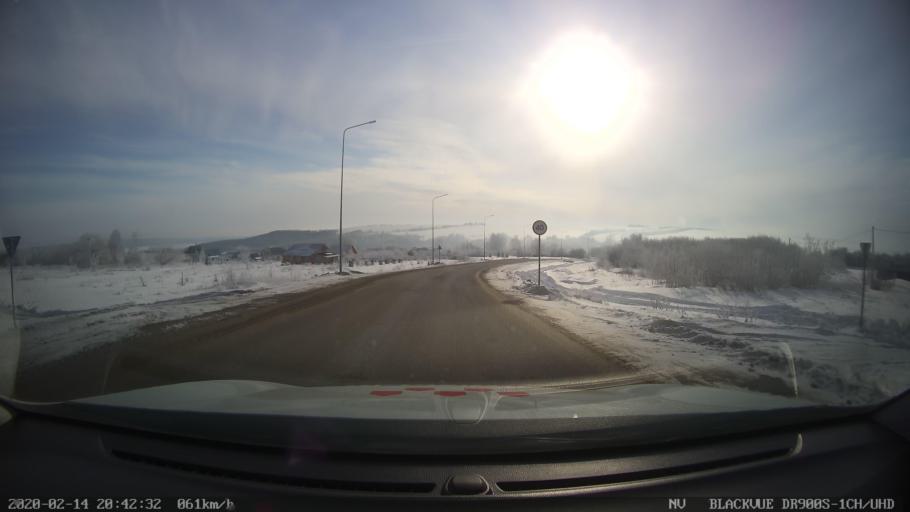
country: RU
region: Tatarstan
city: Kuybyshevskiy Zaton
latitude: 55.3164
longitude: 49.1434
